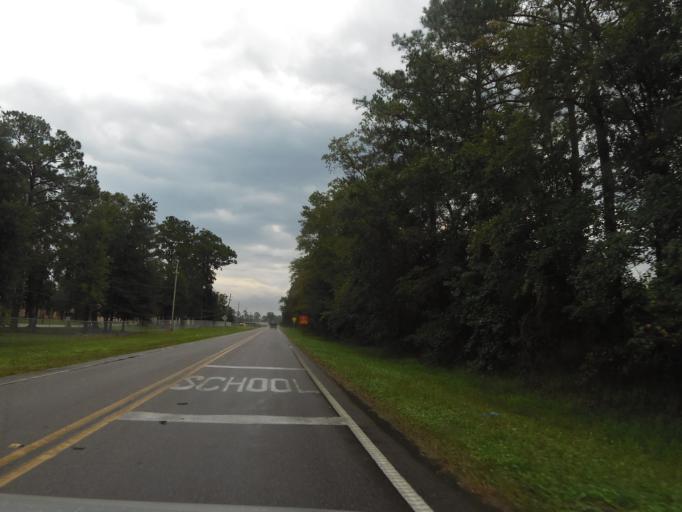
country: US
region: Florida
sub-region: Clay County
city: Middleburg
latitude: 30.0875
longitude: -81.8538
